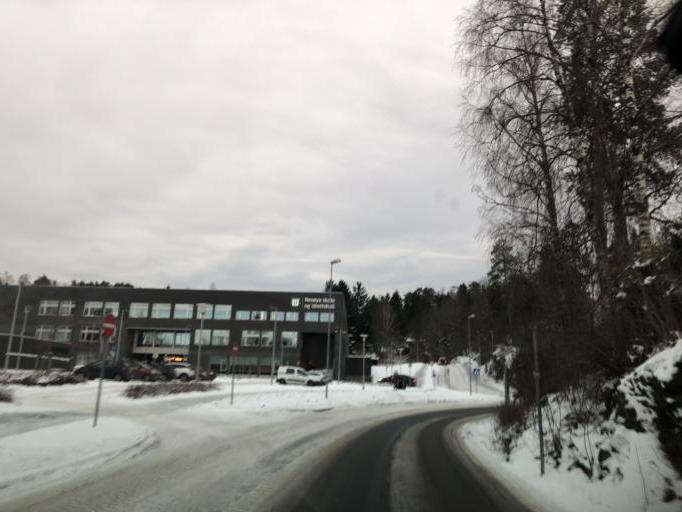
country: NO
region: Akershus
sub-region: Baerum
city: Sandvika
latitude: 59.8701
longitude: 10.5169
